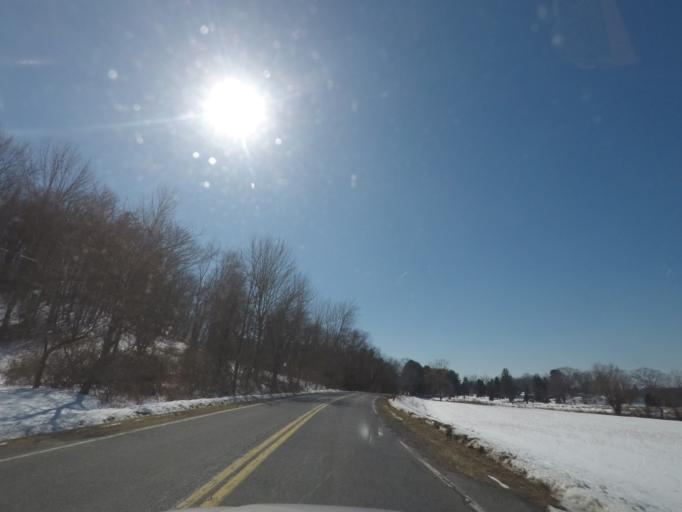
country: US
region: New York
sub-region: Saratoga County
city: Stillwater
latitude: 42.9456
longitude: -73.6266
